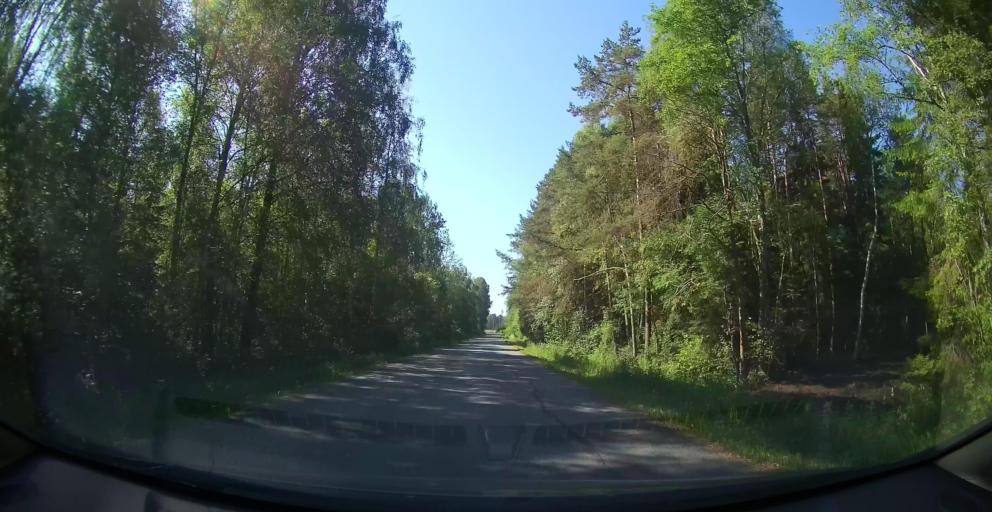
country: EE
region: Harju
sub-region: Raasiku vald
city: Raasiku
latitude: 59.2384
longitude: 25.1731
